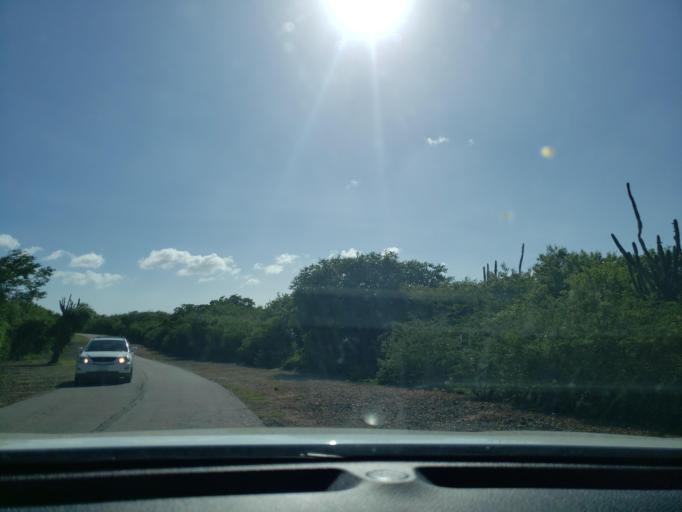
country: CW
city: Dorp Soto
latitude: 12.3495
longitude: -69.1526
